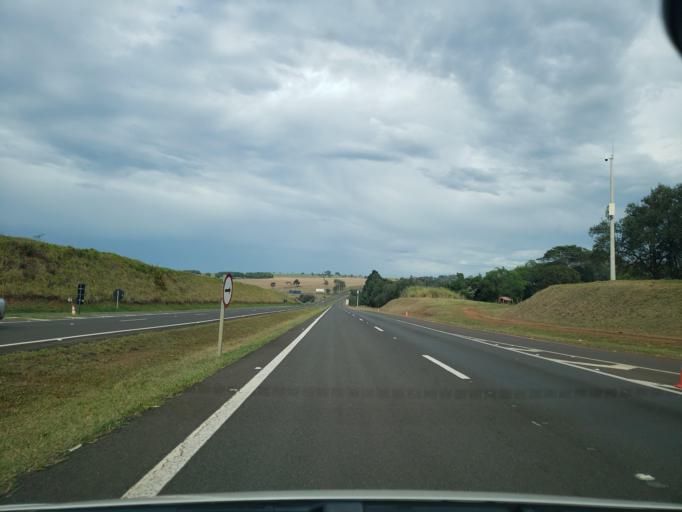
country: BR
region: Sao Paulo
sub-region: Dois Corregos
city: Dois Corregos
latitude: -22.2510
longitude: -48.3606
